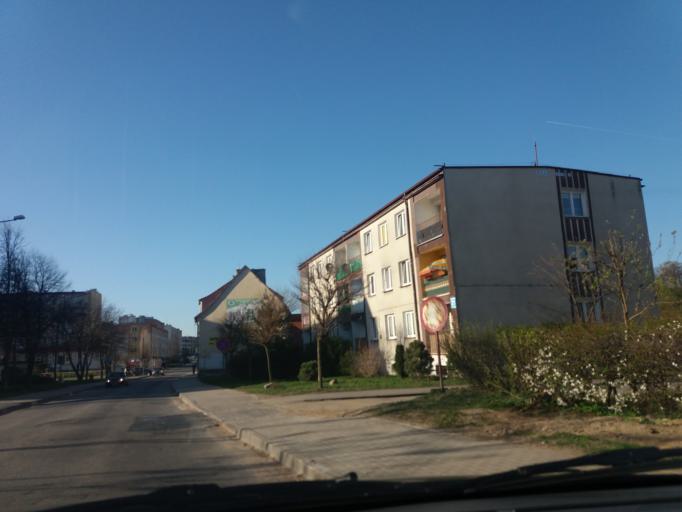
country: PL
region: Warmian-Masurian Voivodeship
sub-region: Powiat nidzicki
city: Nidzica
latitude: 53.3556
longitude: 20.4264
